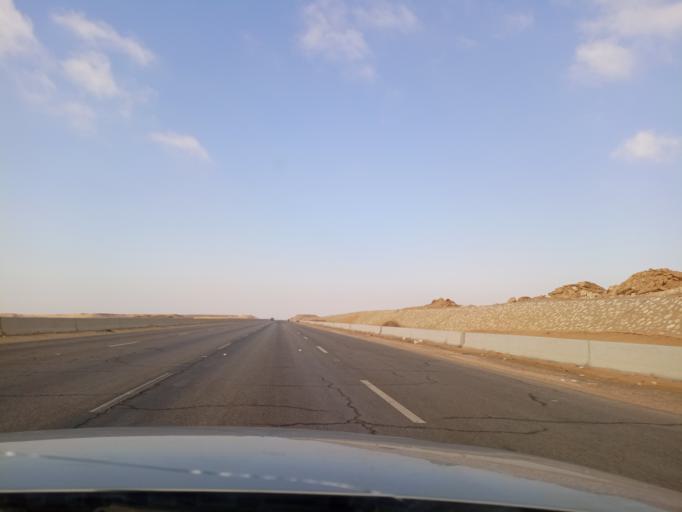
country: EG
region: Al Jizah
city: Al `Ayyat
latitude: 29.6680
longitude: 31.1826
